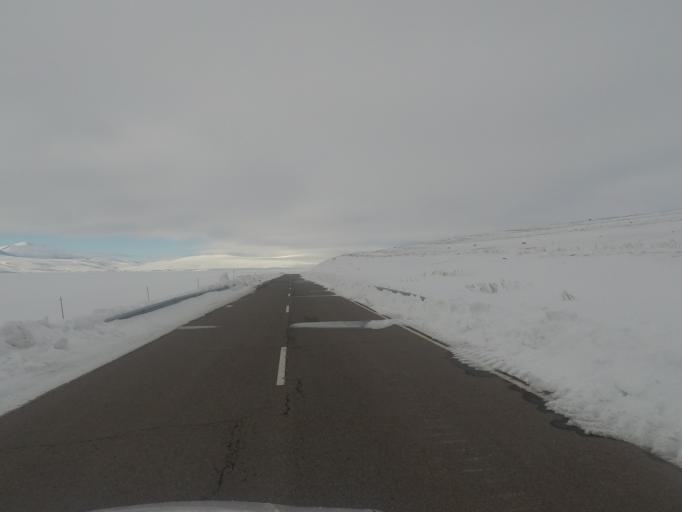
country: GE
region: Samtskhe-Javakheti
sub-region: Ninotsminda
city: Ninotsminda
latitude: 41.4193
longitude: 43.8334
